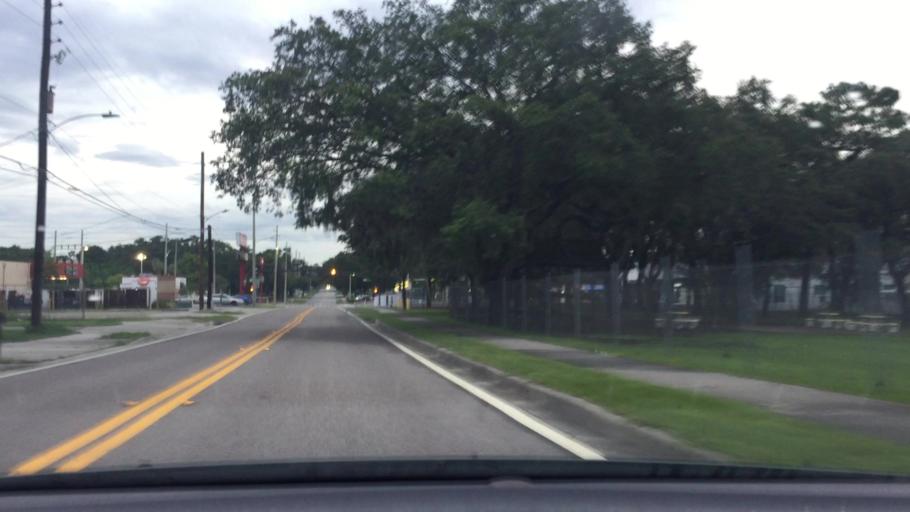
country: US
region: Florida
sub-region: Orange County
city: Orlovista
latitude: 28.5507
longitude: -81.4645
